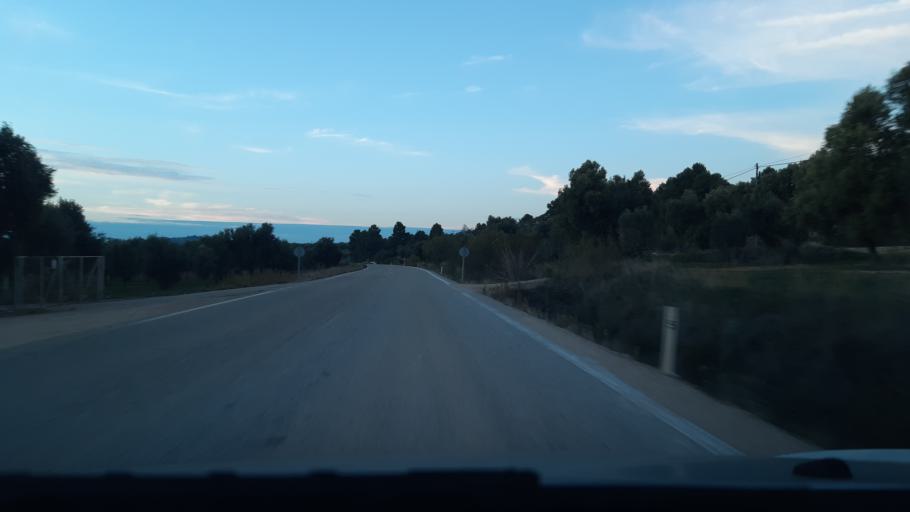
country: ES
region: Aragon
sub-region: Provincia de Teruel
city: Valderrobres
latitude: 40.8537
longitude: 0.1731
